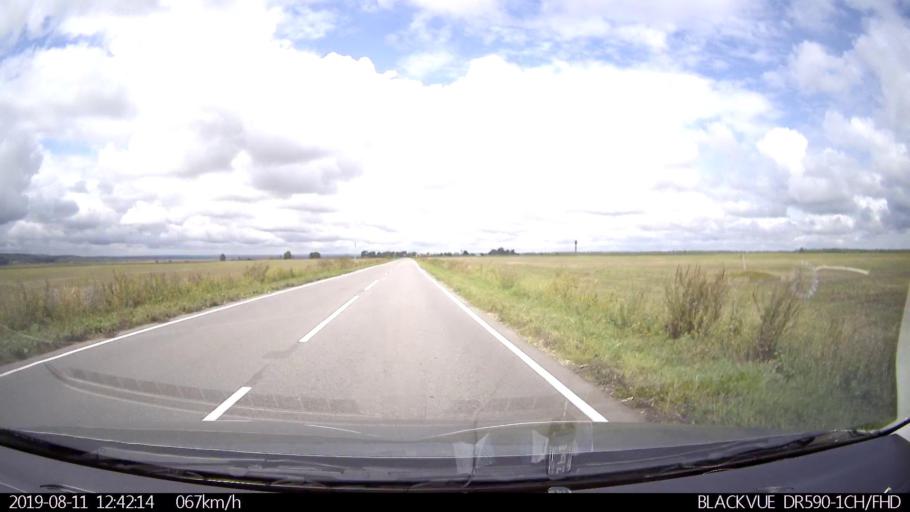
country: RU
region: Ulyanovsk
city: Ignatovka
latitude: 53.8443
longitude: 47.7539
